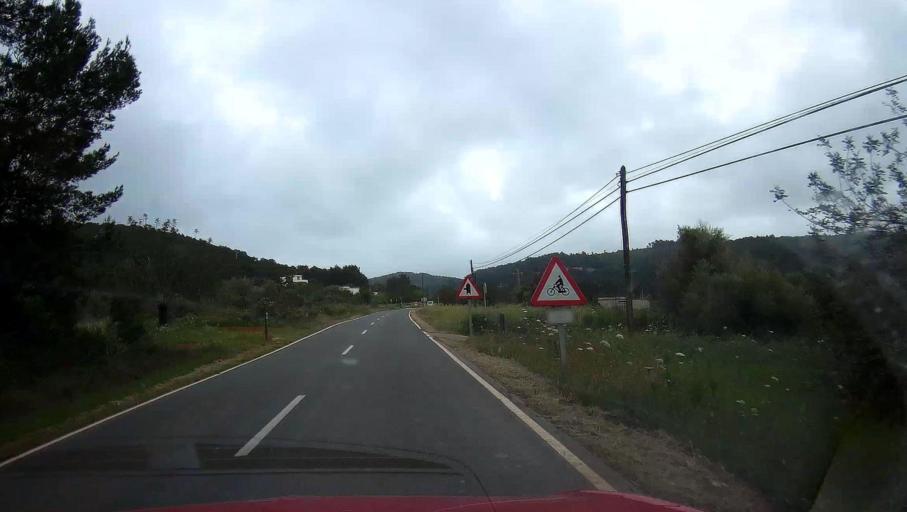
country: ES
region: Balearic Islands
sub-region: Illes Balears
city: Sant Joan de Labritja
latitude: 39.0692
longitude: 1.4910
